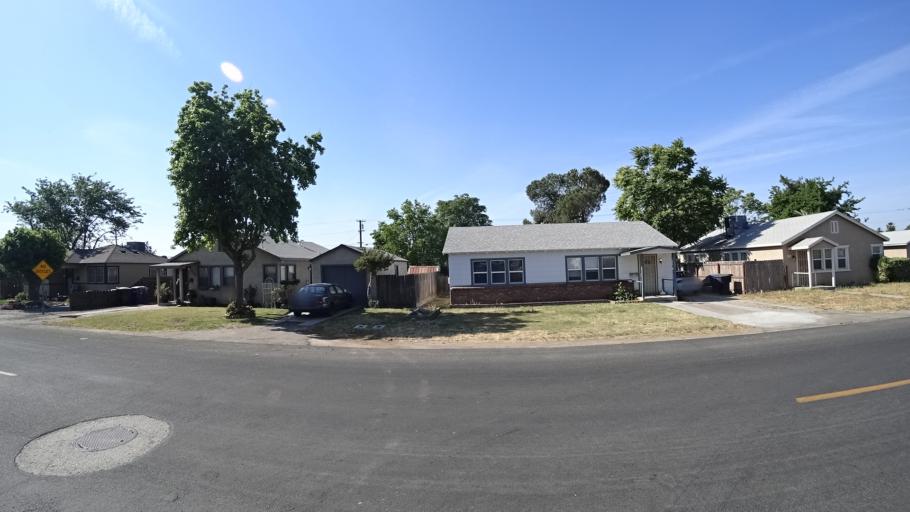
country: US
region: California
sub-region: Kings County
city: Hanford
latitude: 36.3322
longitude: -119.6346
